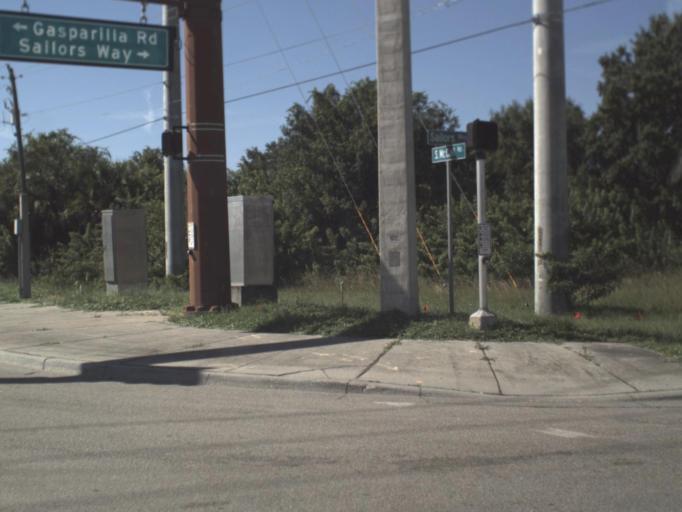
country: US
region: Florida
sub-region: Charlotte County
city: Rotonda
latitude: 26.9336
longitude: -82.2222
